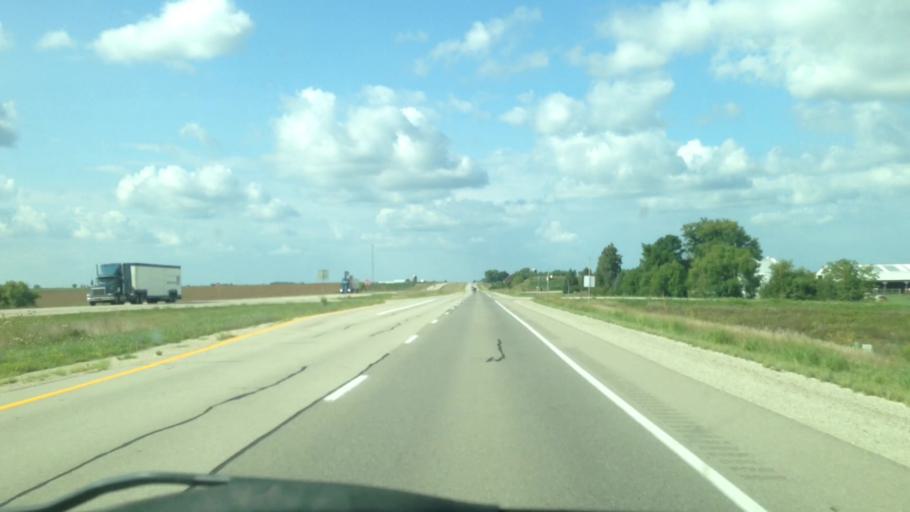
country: US
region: Iowa
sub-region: Henry County
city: Mount Pleasant
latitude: 40.7979
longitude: -91.5642
